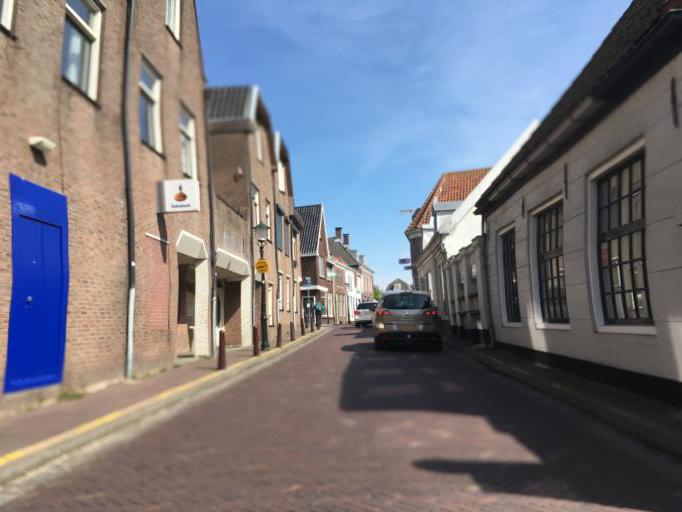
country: NL
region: North Holland
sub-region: Gemeente Weesp
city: Weesp
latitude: 52.3304
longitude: 5.0676
